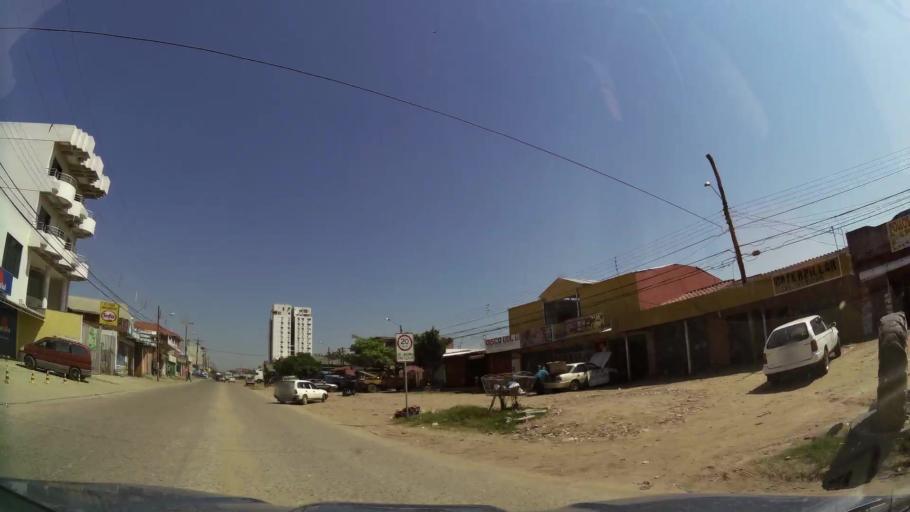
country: BO
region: Santa Cruz
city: Santa Cruz de la Sierra
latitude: -17.7371
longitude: -63.1454
